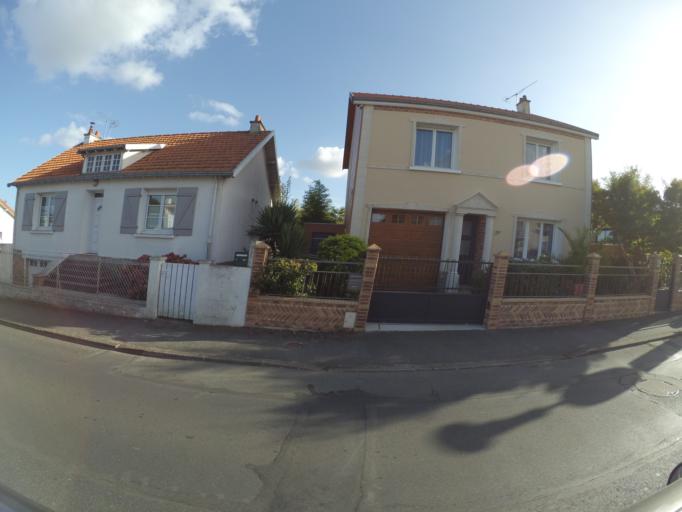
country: FR
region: Pays de la Loire
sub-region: Departement de la Vendee
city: Montaigu
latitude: 46.9782
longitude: -1.3077
